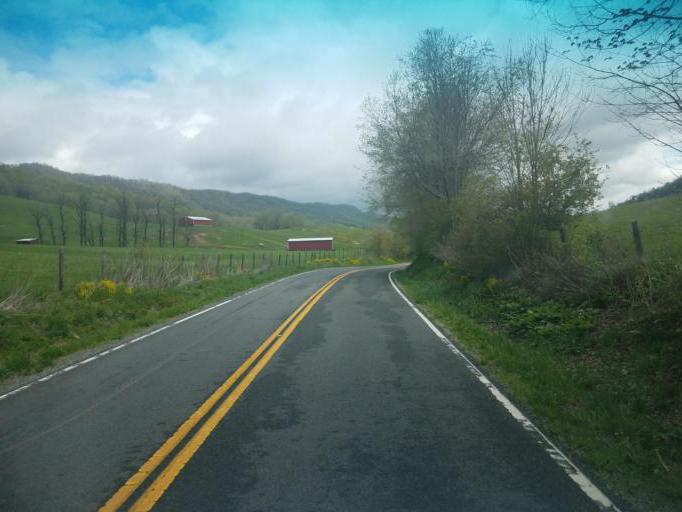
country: US
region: Virginia
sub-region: Smyth County
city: Atkins
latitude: 36.9931
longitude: -81.3829
